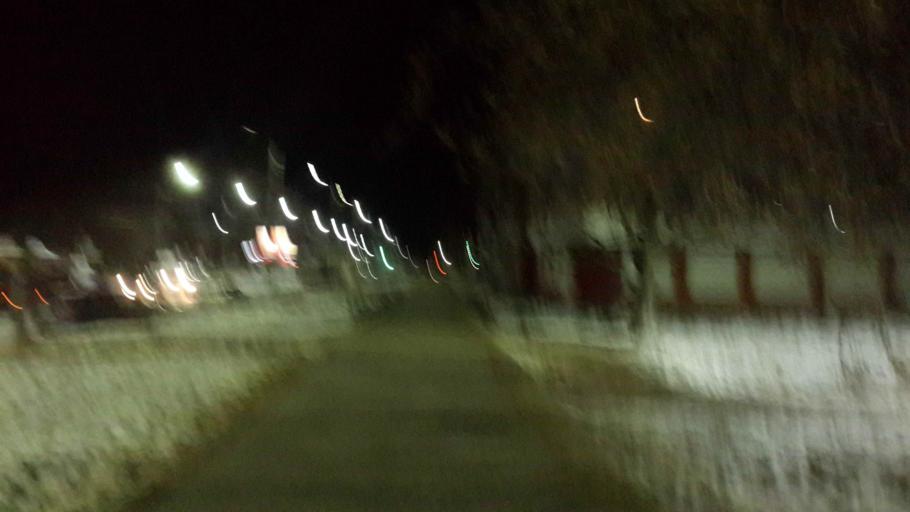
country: RU
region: Tula
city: Tula
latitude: 54.2187
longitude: 37.6186
